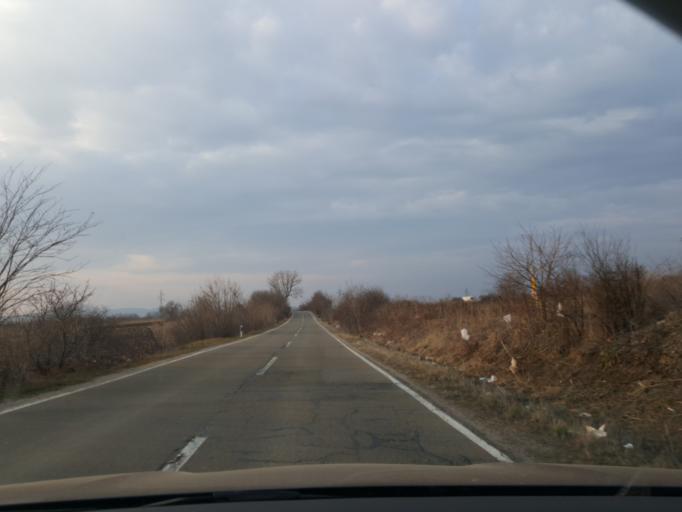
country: RS
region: Central Serbia
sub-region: Nisavski Okrug
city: Aleksinac
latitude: 43.5833
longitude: 21.6564
